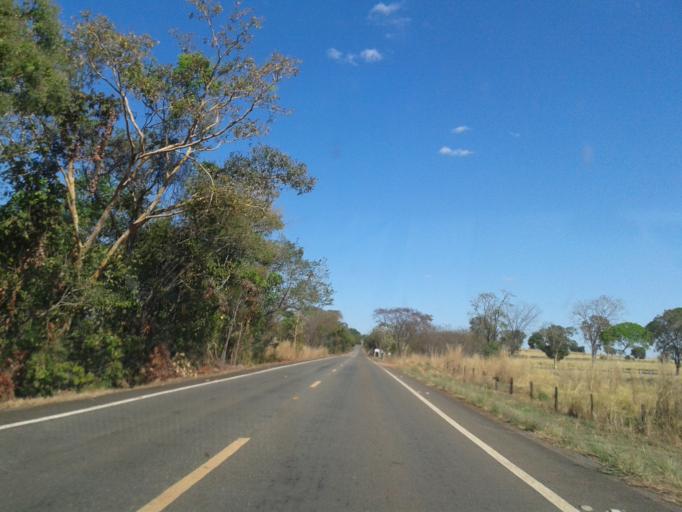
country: BR
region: Goias
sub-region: Sao Miguel Do Araguaia
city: Sao Miguel do Araguaia
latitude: -13.9267
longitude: -50.3216
